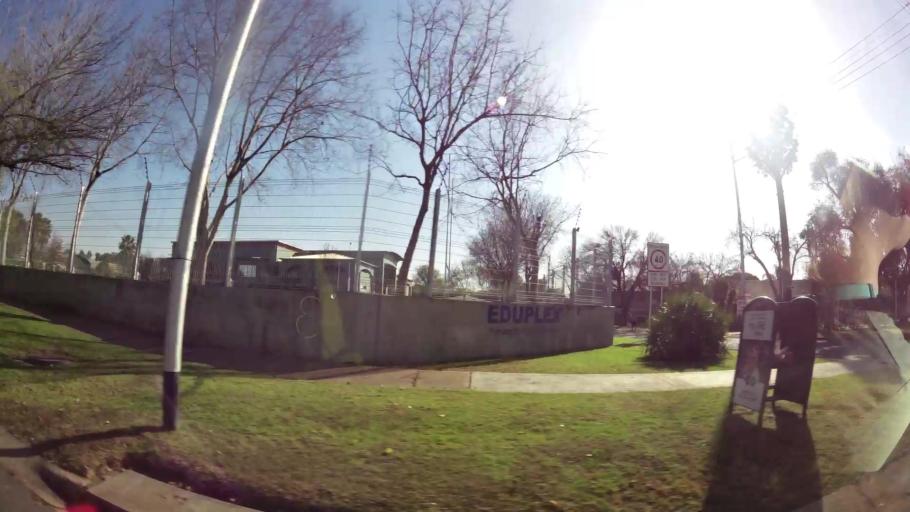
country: ZA
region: Gauteng
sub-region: City of Tshwane Metropolitan Municipality
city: Pretoria
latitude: -25.7238
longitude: 28.2480
